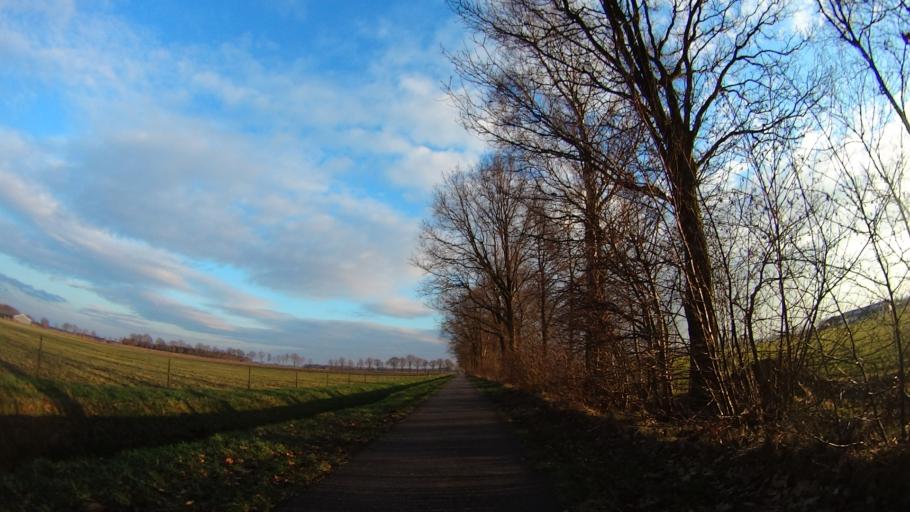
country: NL
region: Drenthe
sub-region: Gemeente Coevorden
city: Sleen
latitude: 52.7898
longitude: 6.7793
